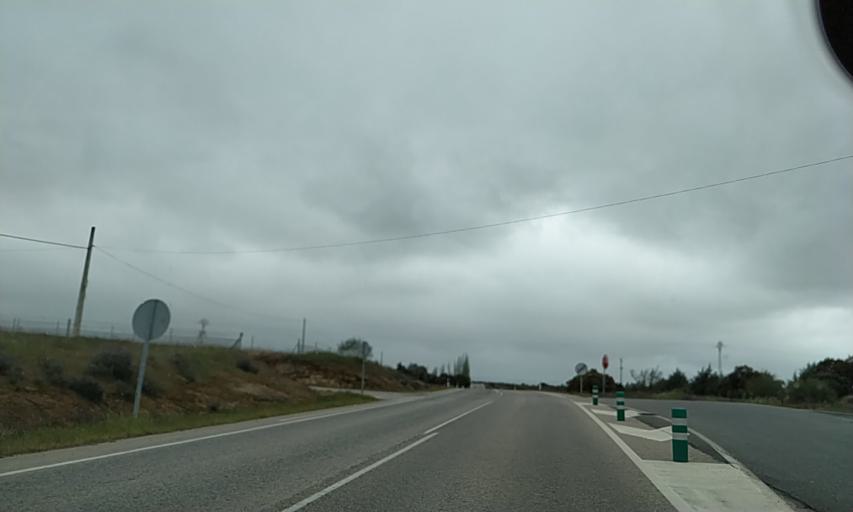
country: ES
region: Extremadura
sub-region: Provincia de Caceres
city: Malpartida de Caceres
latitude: 39.3822
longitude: -6.4441
